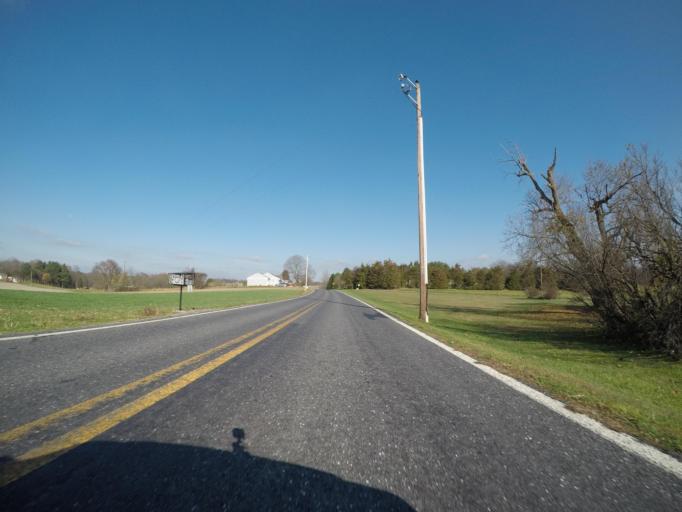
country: US
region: Maryland
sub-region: Carroll County
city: Hampstead
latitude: 39.5450
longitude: -76.8779
